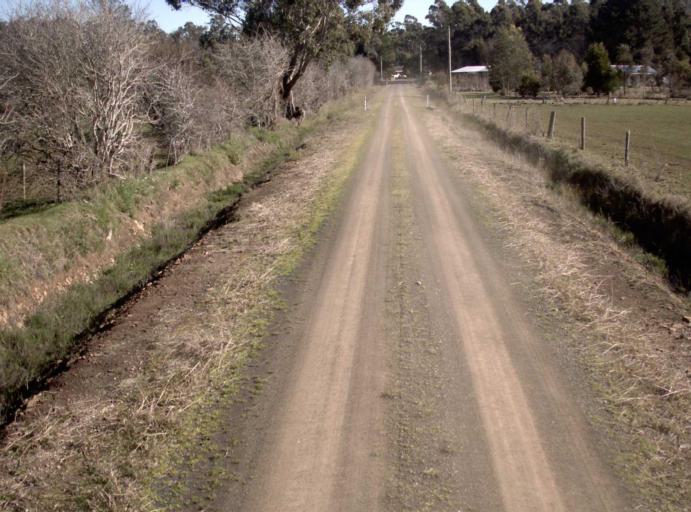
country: AU
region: Tasmania
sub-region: Launceston
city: Mayfield
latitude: -41.2543
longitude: 147.1551
